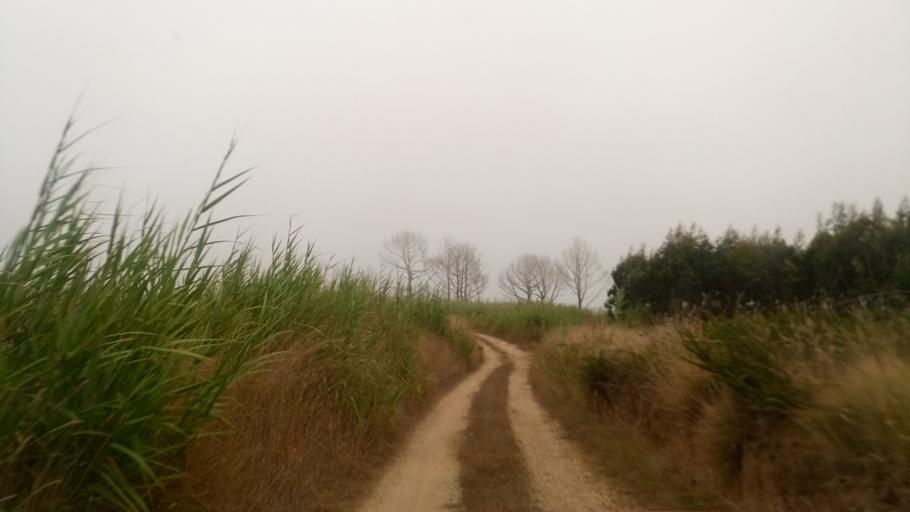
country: PT
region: Leiria
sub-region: Caldas da Rainha
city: Caldas da Rainha
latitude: 39.4673
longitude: -9.1971
